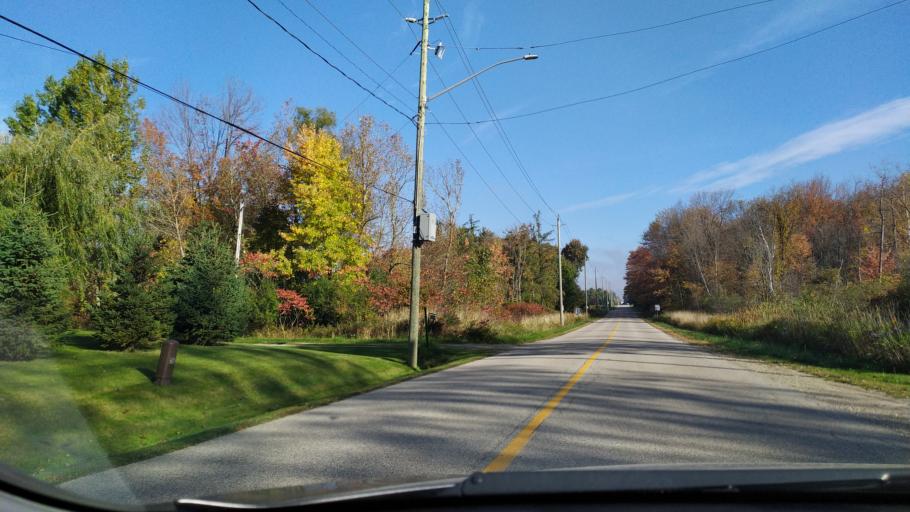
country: CA
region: Ontario
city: Waterloo
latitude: 43.5001
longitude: -80.6559
